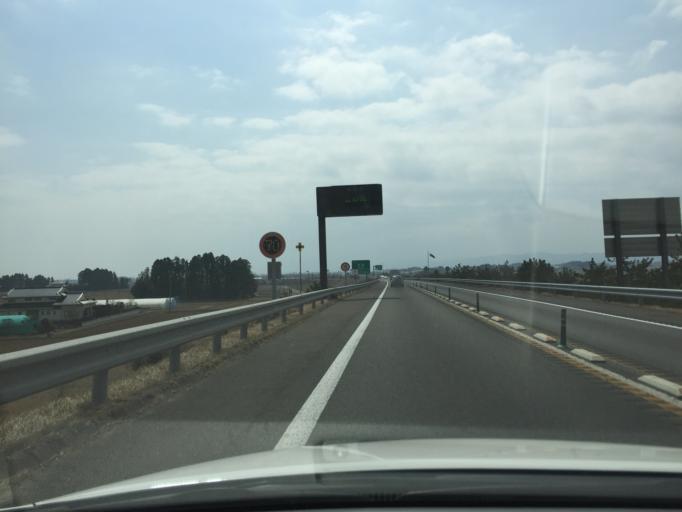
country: JP
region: Miyagi
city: Iwanuma
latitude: 38.0927
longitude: 140.8876
